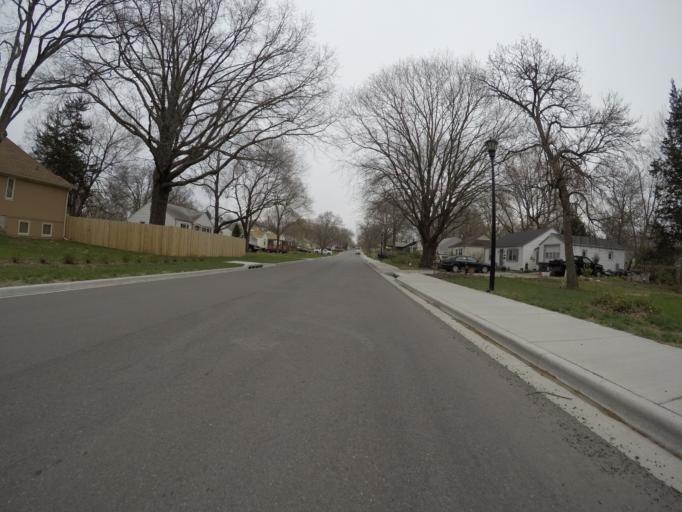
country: US
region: Kansas
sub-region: Johnson County
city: Olathe
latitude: 38.8791
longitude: -94.8092
